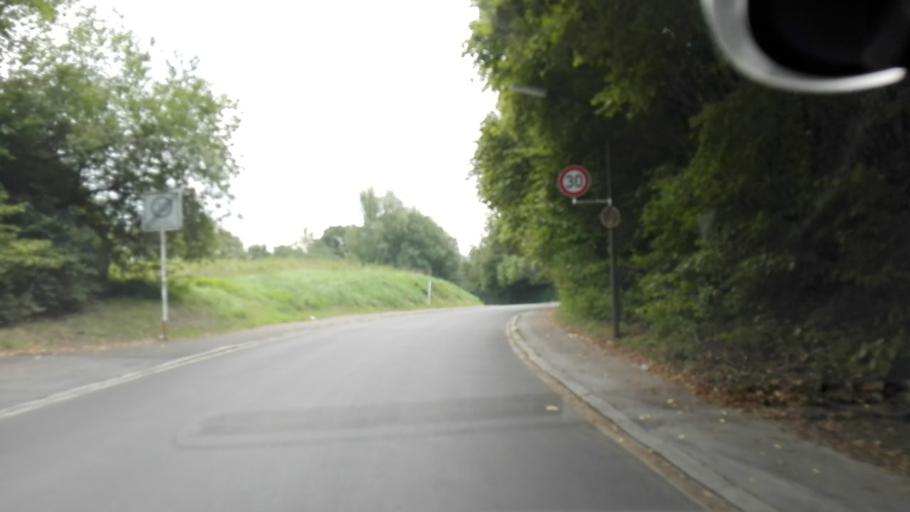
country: DE
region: North Rhine-Westphalia
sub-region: Regierungsbezirk Arnsberg
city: Dortmund
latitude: 51.4878
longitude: 7.4236
